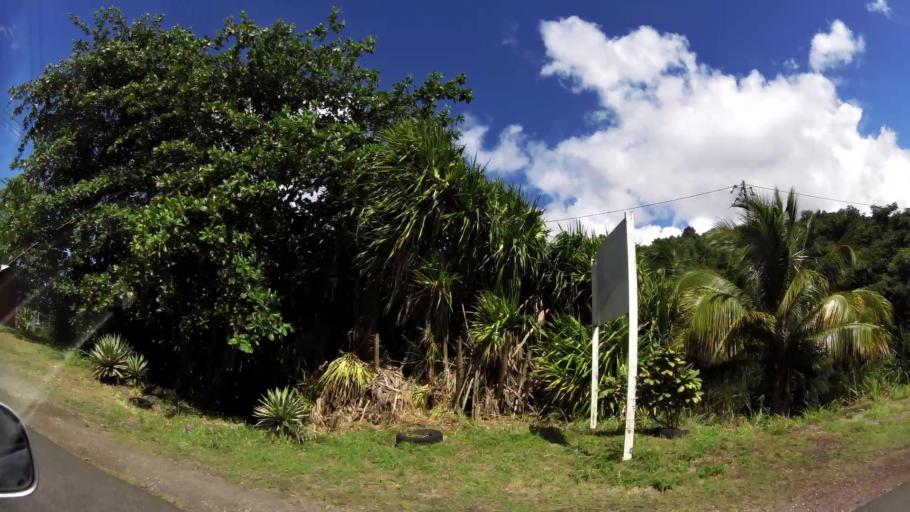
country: GD
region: Saint John
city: Gouyave
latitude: 12.1589
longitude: -61.7320
